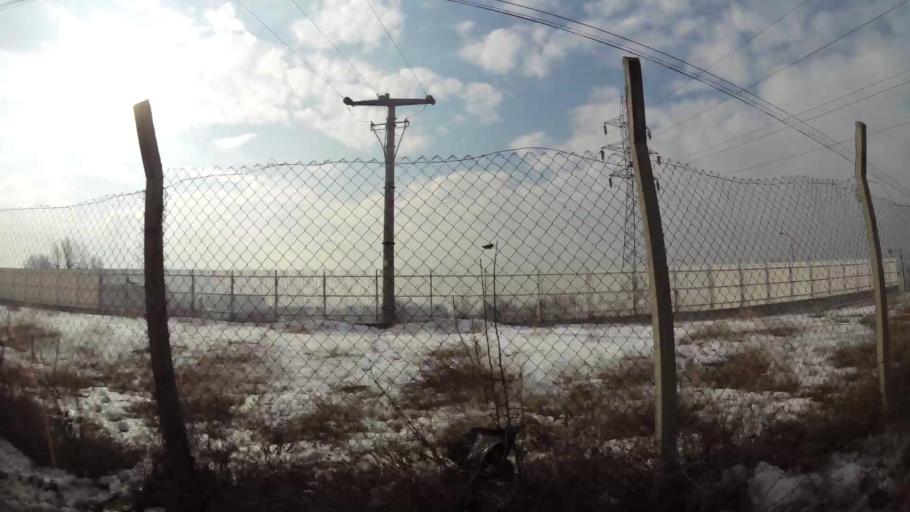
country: MK
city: Krushopek
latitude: 42.0175
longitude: 21.3671
